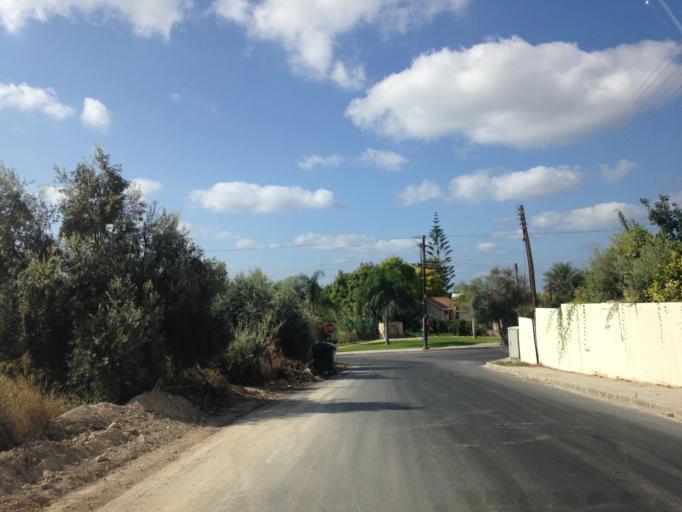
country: CY
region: Pafos
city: Pegeia
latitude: 34.8739
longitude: 32.3706
